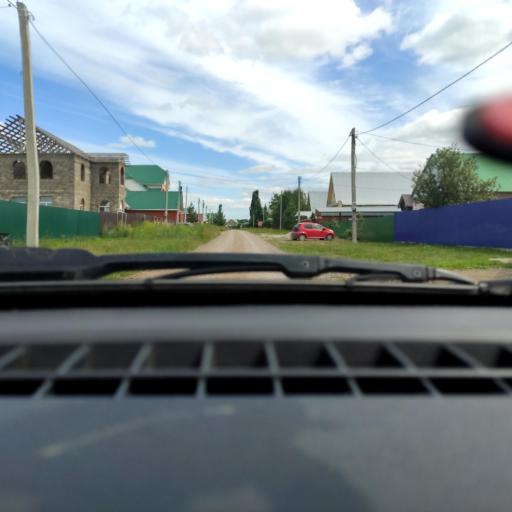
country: RU
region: Bashkortostan
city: Iglino
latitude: 54.7871
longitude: 56.2438
